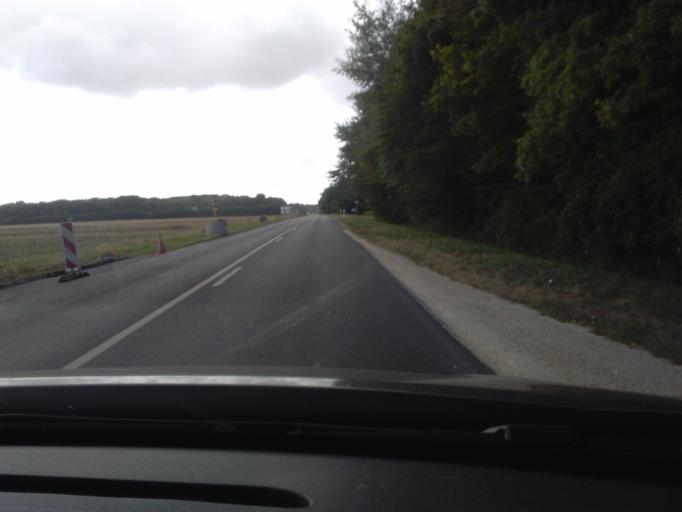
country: FR
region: Centre
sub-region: Departement du Loir-et-Cher
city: Cormeray
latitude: 47.5118
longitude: 1.4021
